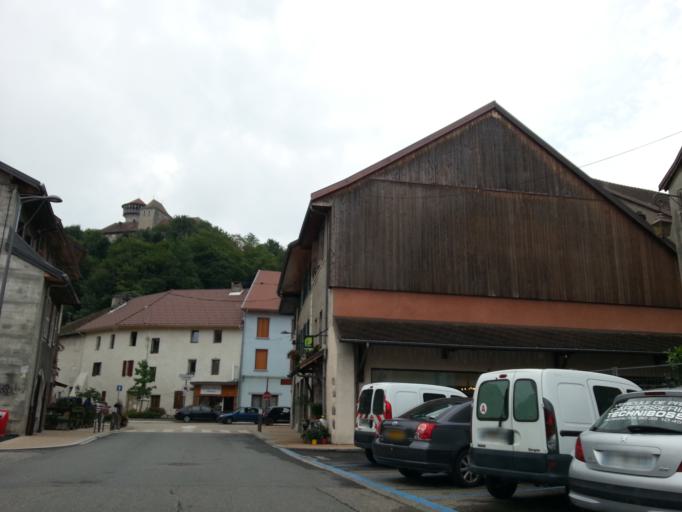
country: FR
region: Rhone-Alpes
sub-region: Departement de la Haute-Savoie
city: Faverges
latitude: 45.7472
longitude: 6.2957
